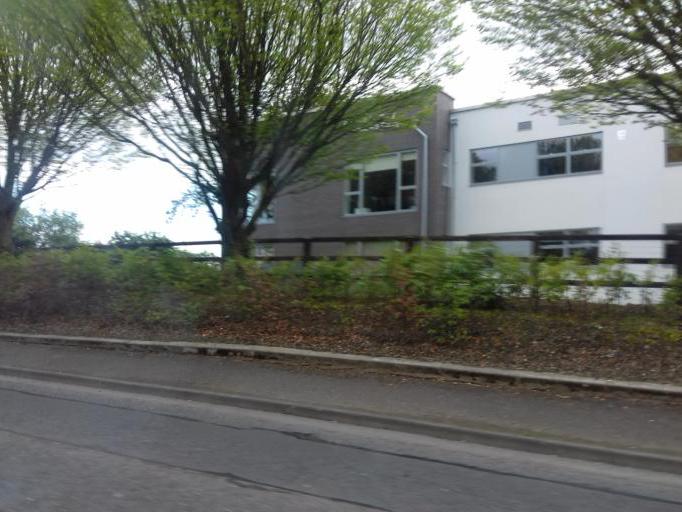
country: IE
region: Leinster
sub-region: Kildare
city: Kildare
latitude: 53.1543
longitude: -6.9016
